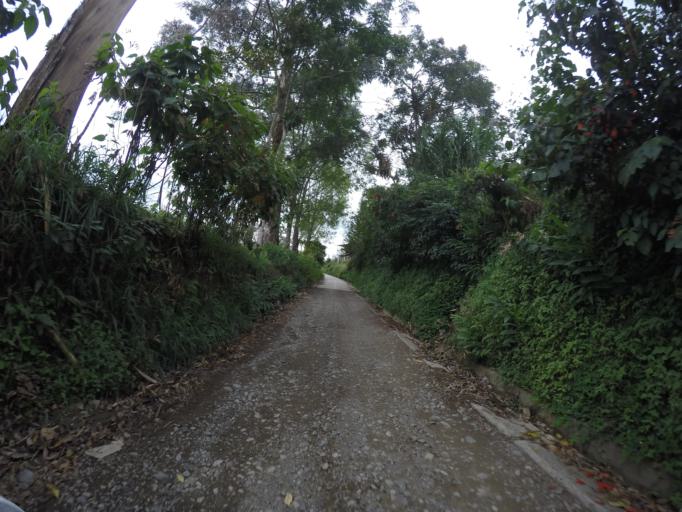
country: CO
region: Quindio
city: Filandia
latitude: 4.6387
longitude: -75.6787
